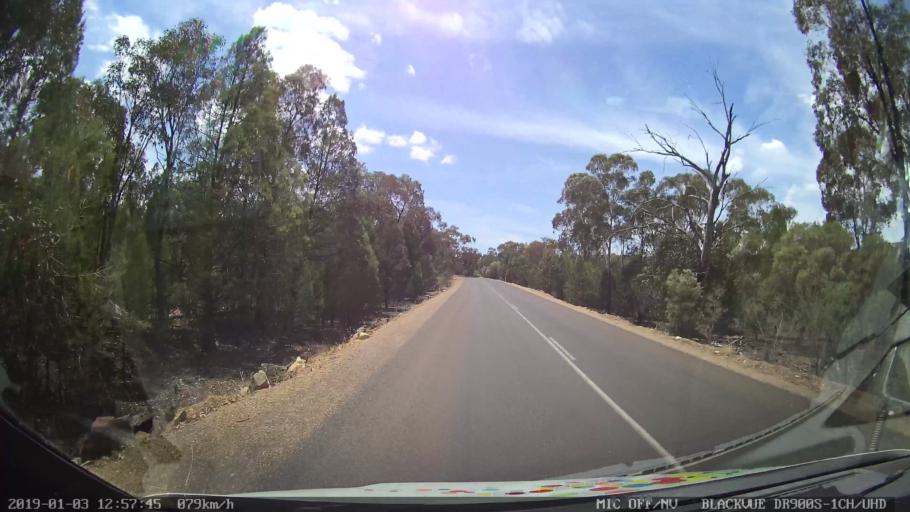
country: AU
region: New South Wales
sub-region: Cabonne
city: Canowindra
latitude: -33.6460
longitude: 148.3661
